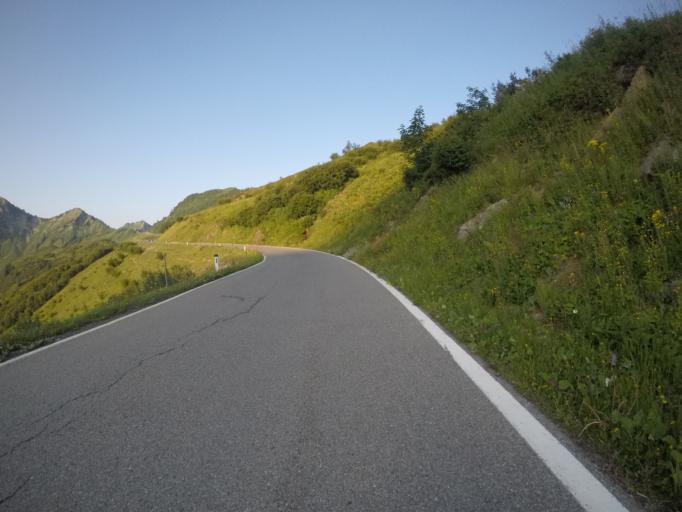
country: AT
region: Vorarlberg
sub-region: Politischer Bezirk Bregenz
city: Damuels
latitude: 47.2775
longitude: 9.8376
